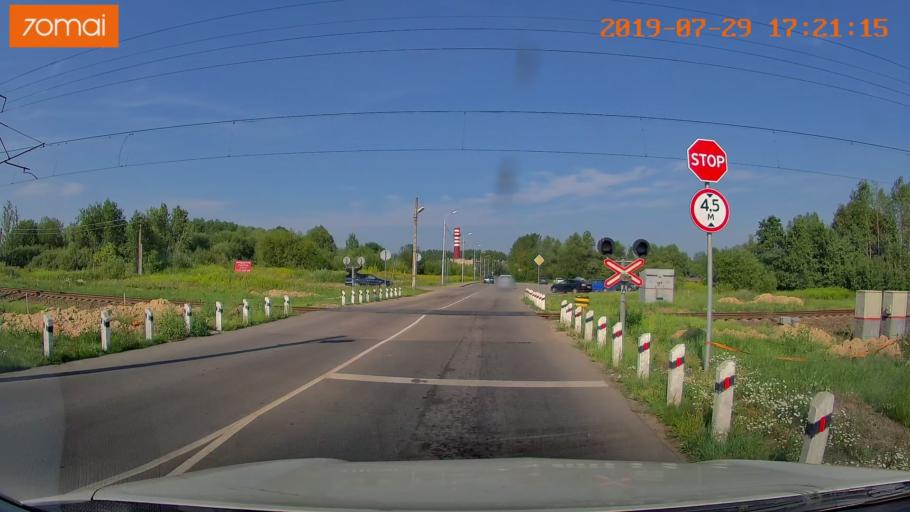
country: RU
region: Kaliningrad
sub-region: Gorod Kaliningrad
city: Kaliningrad
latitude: 54.7690
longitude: 20.4281
